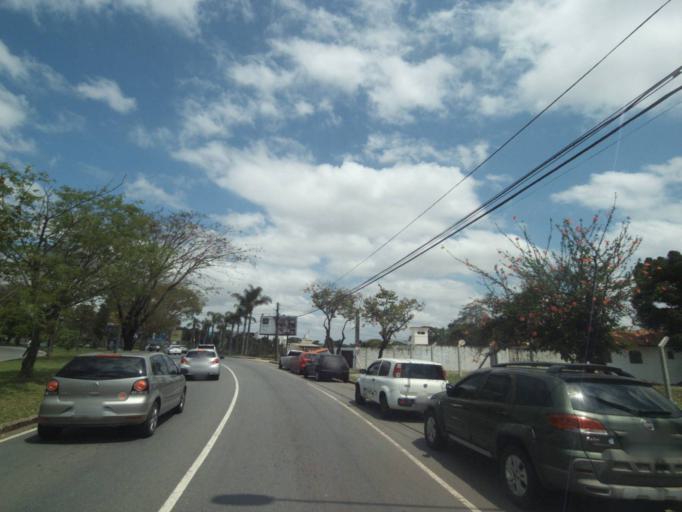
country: BR
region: Parana
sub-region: Curitiba
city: Curitiba
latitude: -25.4161
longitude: -49.2418
